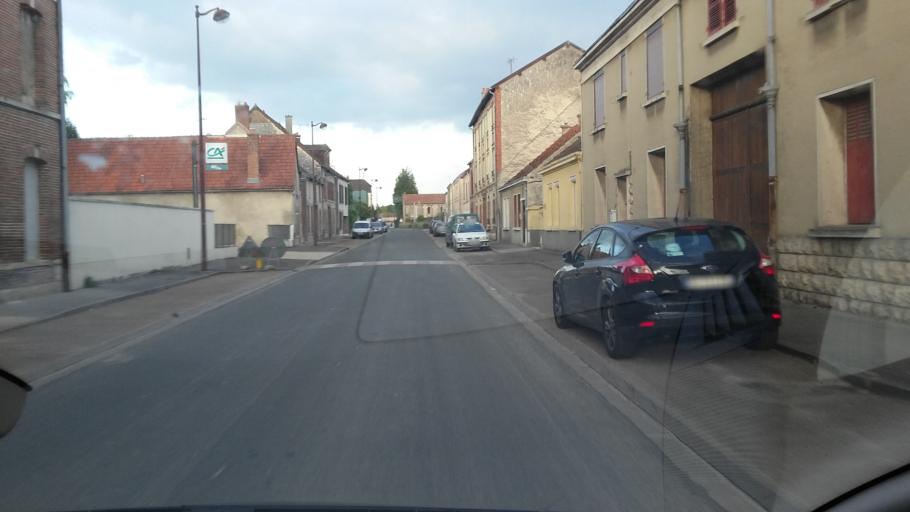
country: FR
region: Champagne-Ardenne
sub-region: Departement de la Marne
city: Fere-Champenoise
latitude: 48.7558
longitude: 3.9922
